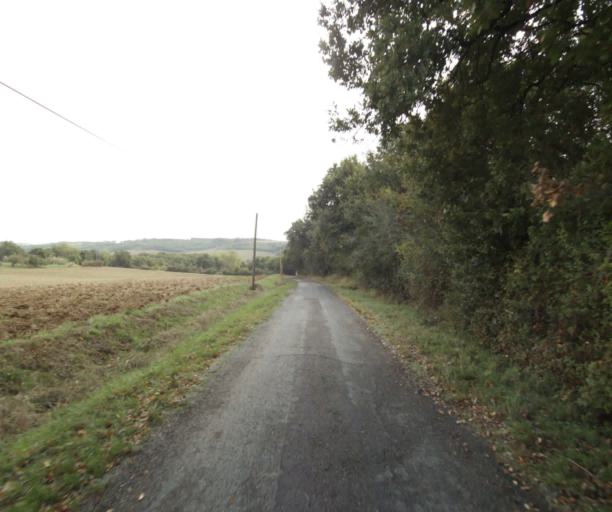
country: FR
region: Midi-Pyrenees
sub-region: Departement du Tarn-et-Garonne
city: Beaumont-de-Lomagne
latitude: 43.8707
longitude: 1.1006
